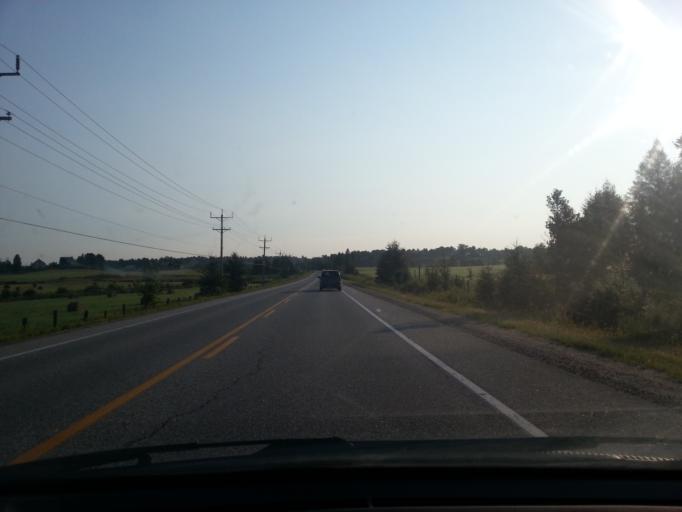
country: CA
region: Quebec
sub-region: Outaouais
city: Wakefield
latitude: 45.9068
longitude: -76.0236
